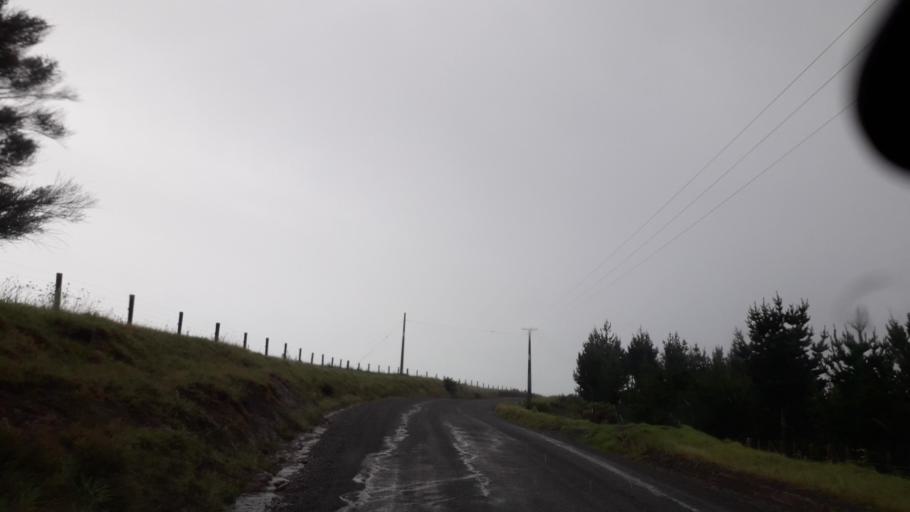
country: NZ
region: Northland
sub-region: Far North District
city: Kerikeri
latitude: -35.1339
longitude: 174.0162
